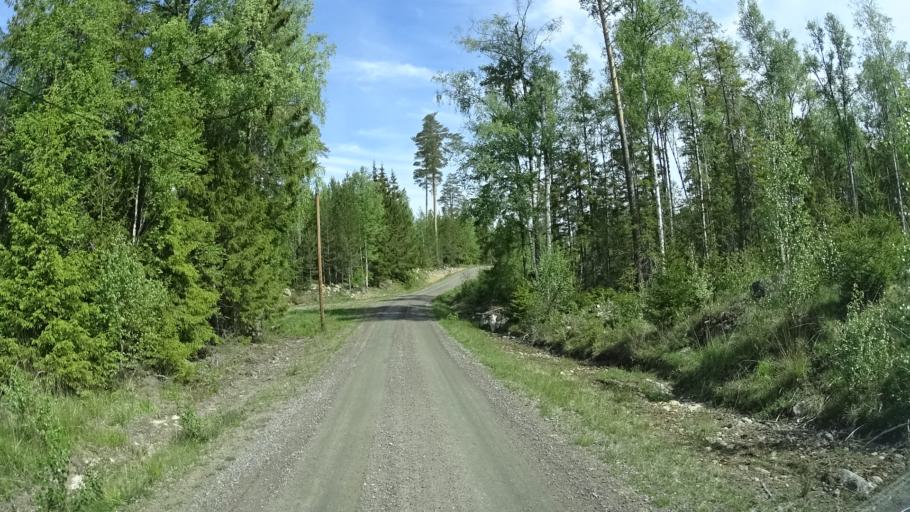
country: SE
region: OEstergoetland
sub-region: Finspangs Kommun
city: Finspang
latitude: 58.7787
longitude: 15.8551
